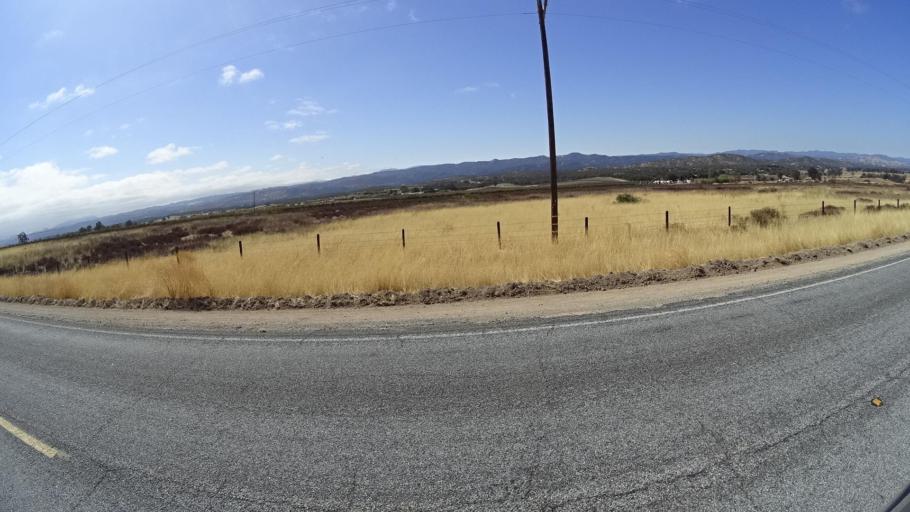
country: US
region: California
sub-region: San Luis Obispo County
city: Lake Nacimiento
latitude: 35.9253
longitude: -121.0403
